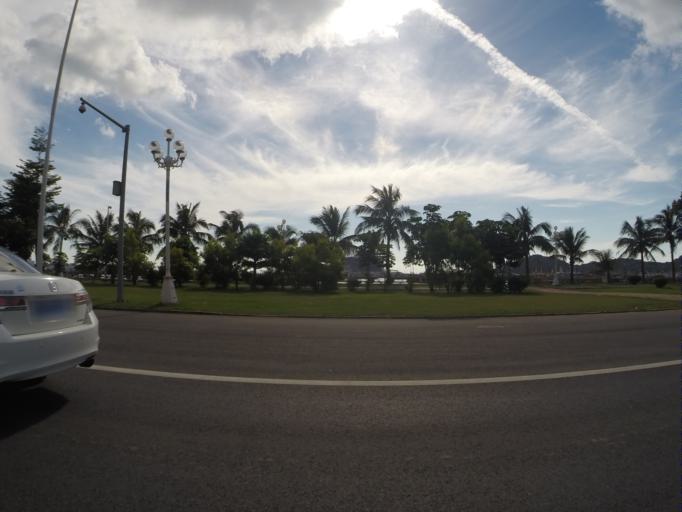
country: CN
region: Guangdong
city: Zhuhai
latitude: 22.2849
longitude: 113.5742
